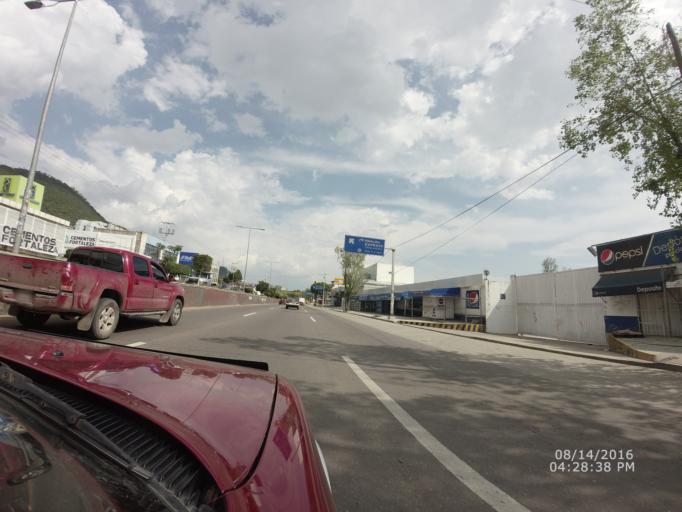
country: MX
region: Oaxaca
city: Oaxaca de Juarez
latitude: 17.0847
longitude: -96.7446
